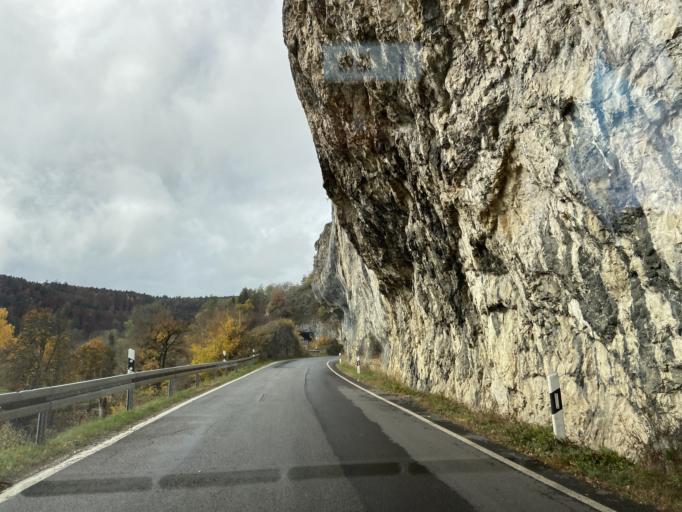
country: DE
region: Baden-Wuerttemberg
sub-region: Tuebingen Region
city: Stetten am Kalten Markt
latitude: 48.0810
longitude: 9.1155
